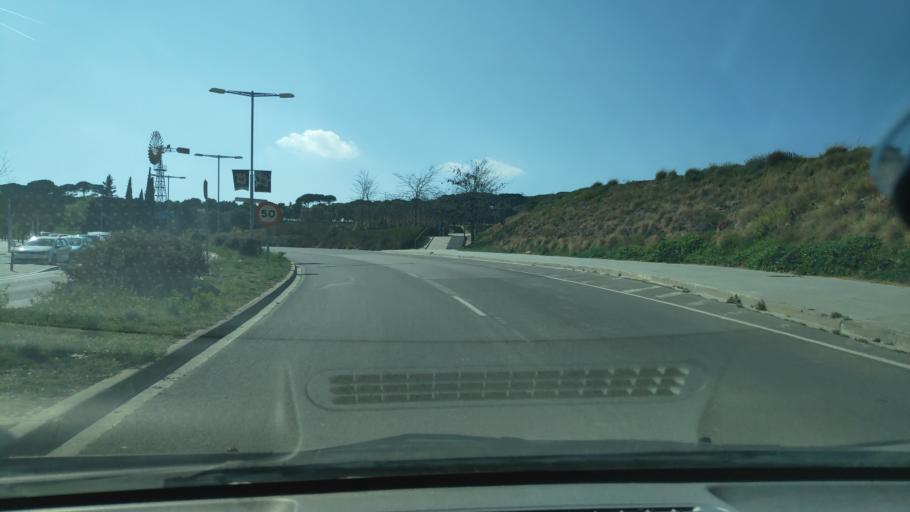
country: ES
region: Catalonia
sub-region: Provincia de Barcelona
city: Mollet del Valles
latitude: 41.5453
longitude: 2.2025
